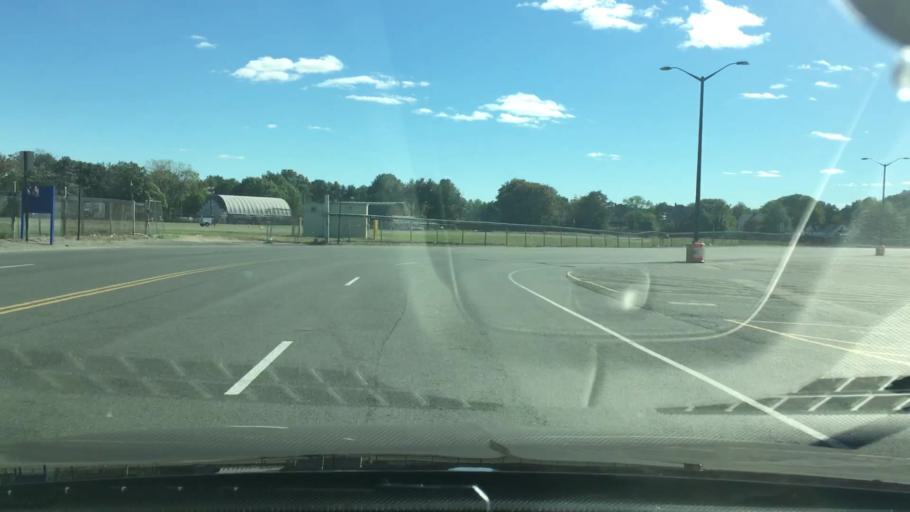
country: US
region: Connecticut
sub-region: Hartford County
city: Wethersfield
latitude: 41.7464
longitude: -72.6293
